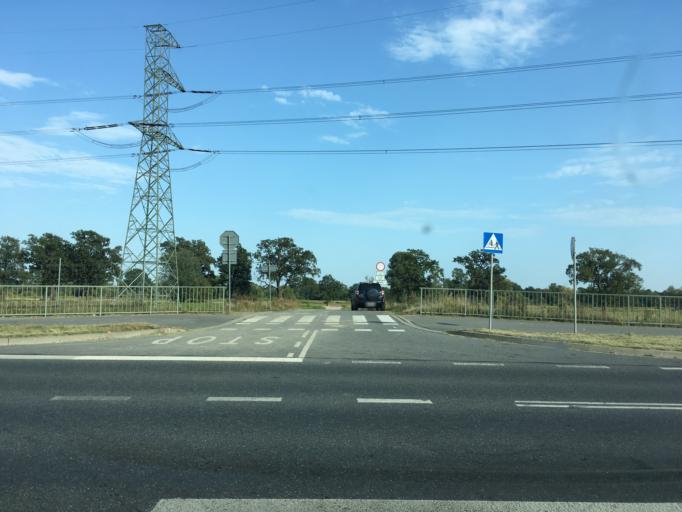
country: PL
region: Lower Silesian Voivodeship
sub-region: Powiat wroclawski
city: Kamieniec Wroclawski
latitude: 51.0679
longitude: 17.1587
